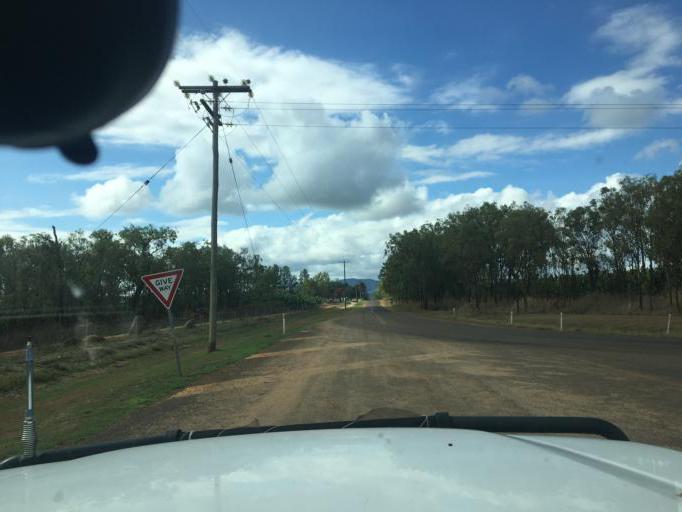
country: AU
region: Queensland
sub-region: Tablelands
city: Mareeba
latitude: -17.0988
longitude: 145.4118
